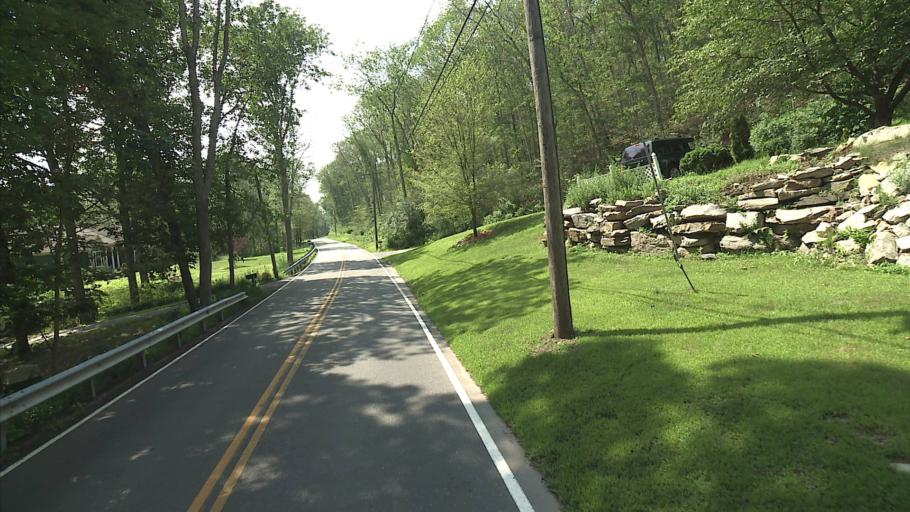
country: US
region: Connecticut
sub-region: Windham County
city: Moosup
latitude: 41.7453
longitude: -71.8540
